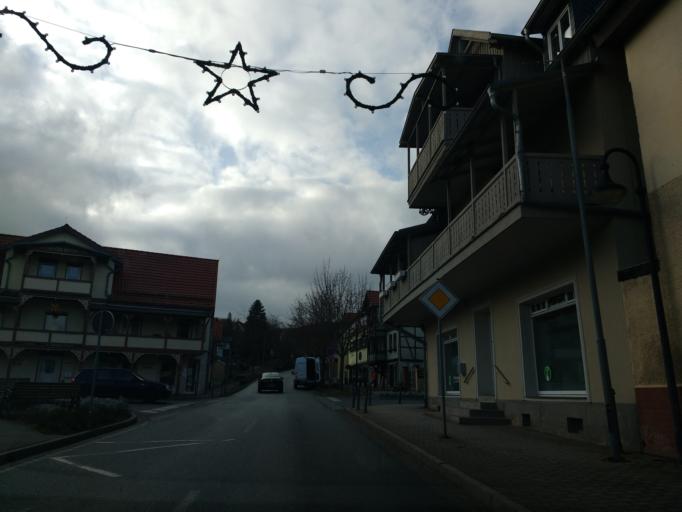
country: DE
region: Saxony-Anhalt
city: Bad Suderode
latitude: 51.7285
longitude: 11.1198
